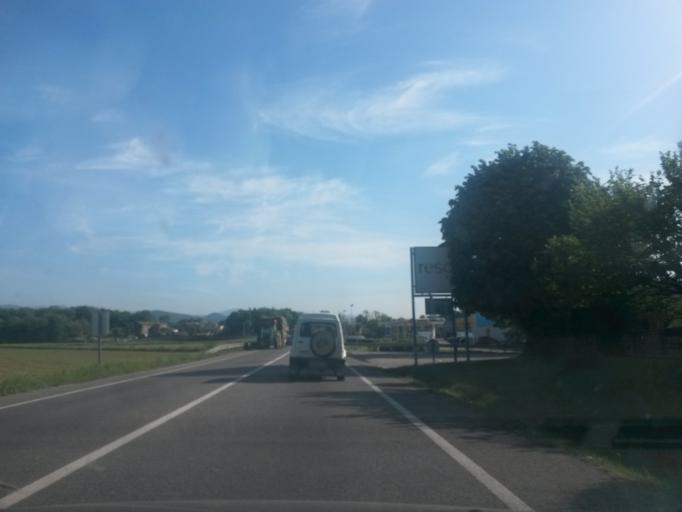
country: ES
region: Catalonia
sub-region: Provincia de Girona
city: Bas
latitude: 42.1540
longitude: 2.4641
